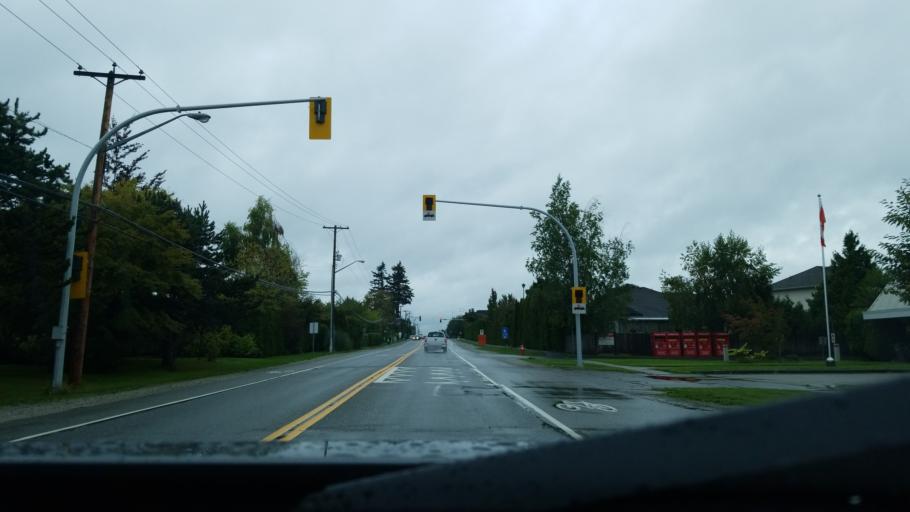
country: CA
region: British Columbia
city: Langley
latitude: 49.1191
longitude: -122.6984
